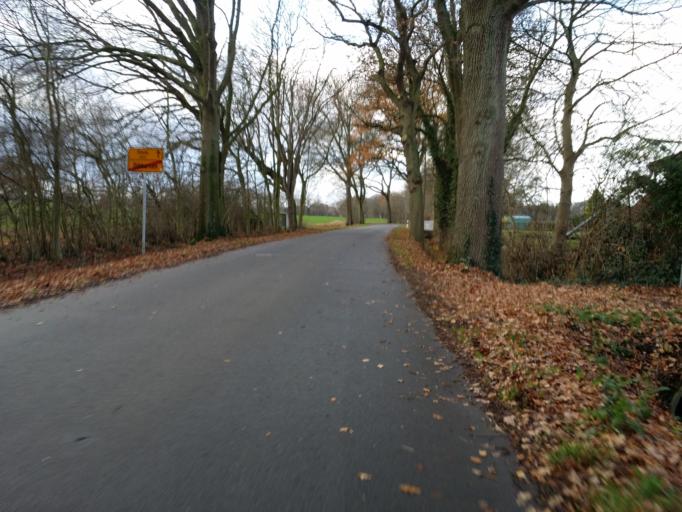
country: DE
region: Lower Saxony
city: Riede
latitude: 52.9768
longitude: 8.9828
